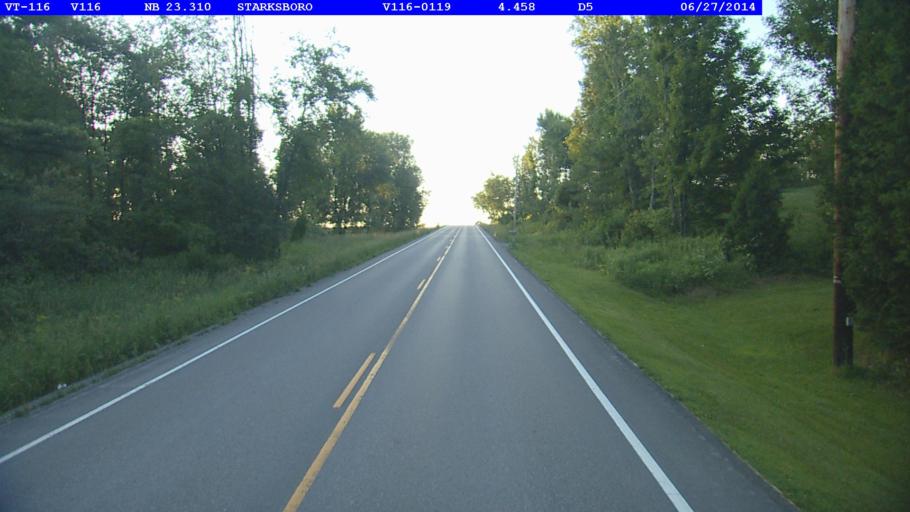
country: US
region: Vermont
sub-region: Chittenden County
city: Hinesburg
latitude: 44.2486
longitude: -73.0613
